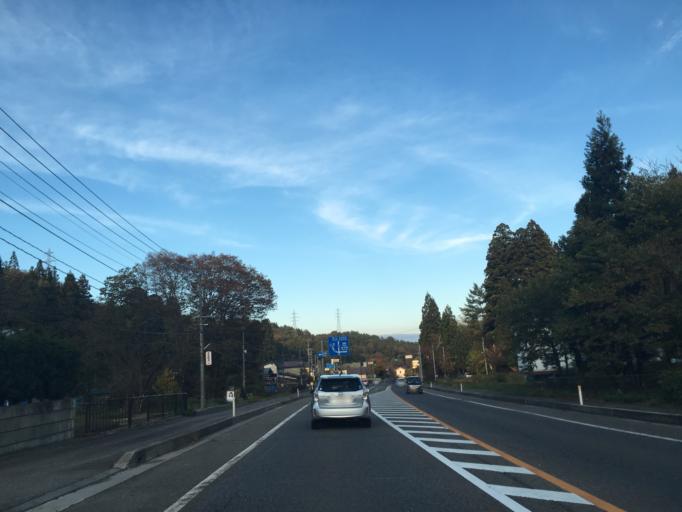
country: JP
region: Fukushima
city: Kitakata
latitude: 37.5704
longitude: 139.7852
